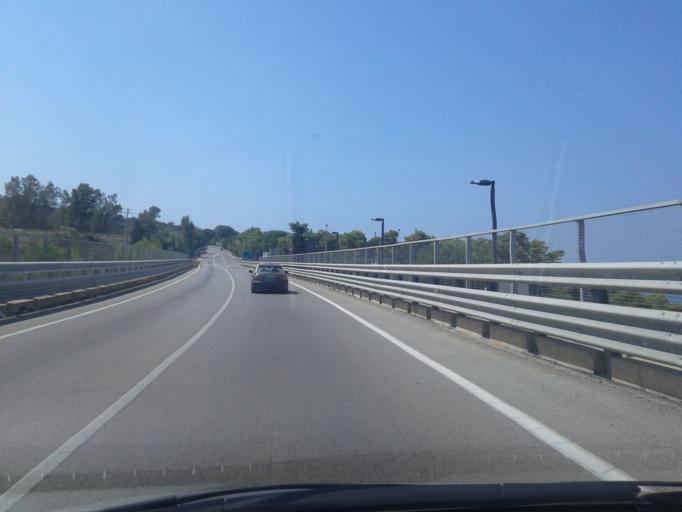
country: IT
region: Sicily
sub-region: Palermo
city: Finale
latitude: 38.0222
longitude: 14.1560
